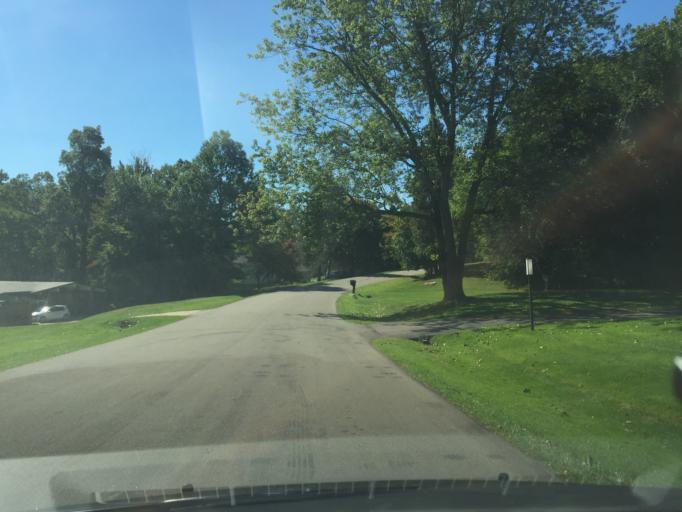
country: US
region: Michigan
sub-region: Oakland County
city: Sylvan Lake
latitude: 42.5743
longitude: -83.3004
